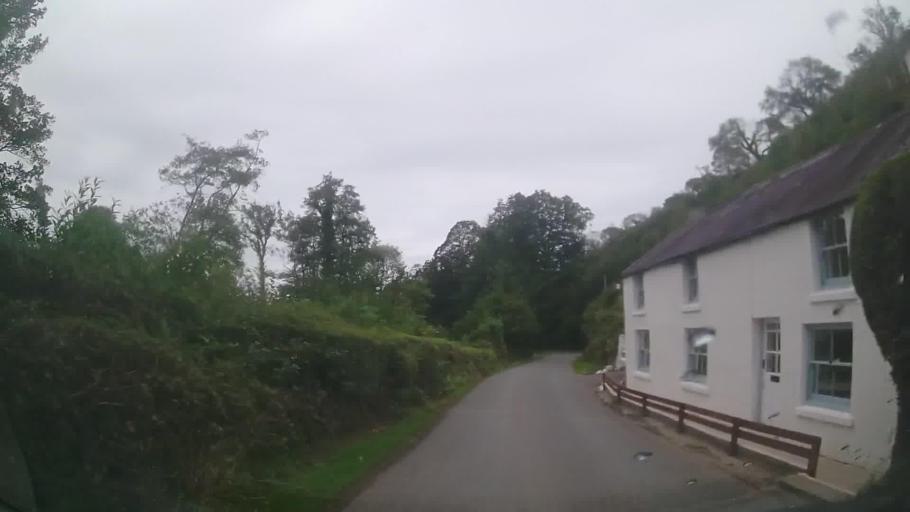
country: GB
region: Wales
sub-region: Pembrokeshire
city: Saundersfoot
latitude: 51.7361
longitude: -4.6576
